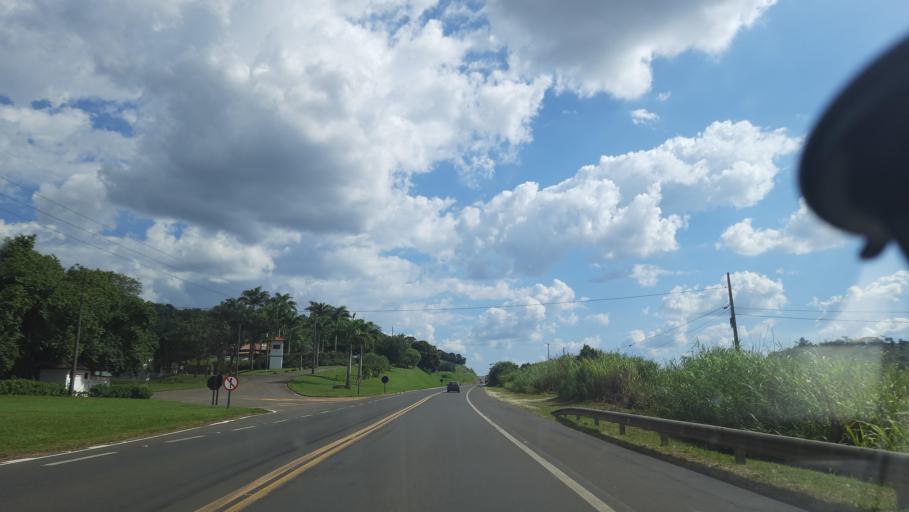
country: BR
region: Sao Paulo
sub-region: Sao Jose Do Rio Pardo
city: Sao Jose do Rio Pardo
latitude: -21.6498
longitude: -46.9104
